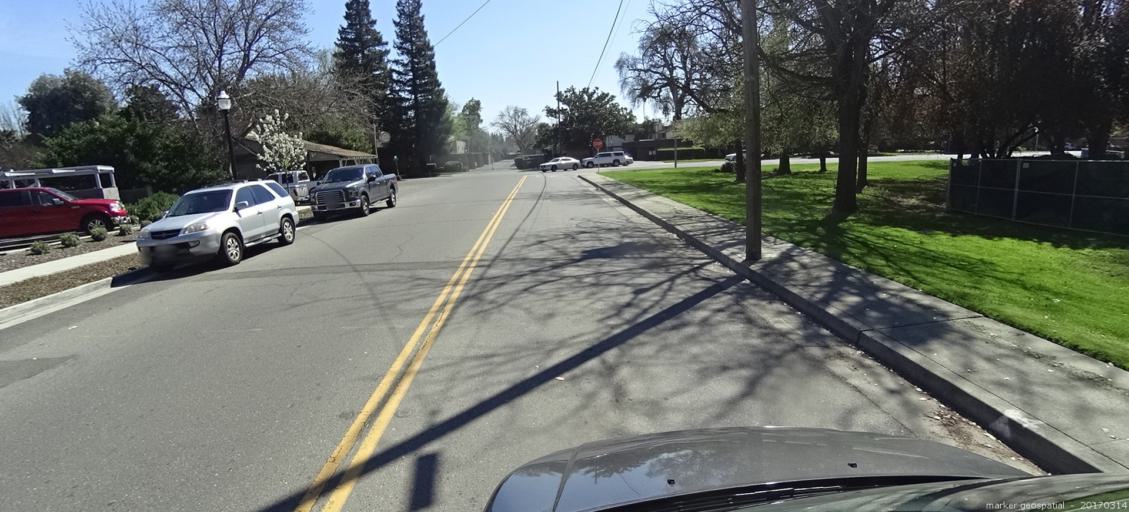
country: US
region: California
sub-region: Yolo County
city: West Sacramento
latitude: 38.5158
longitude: -121.5267
